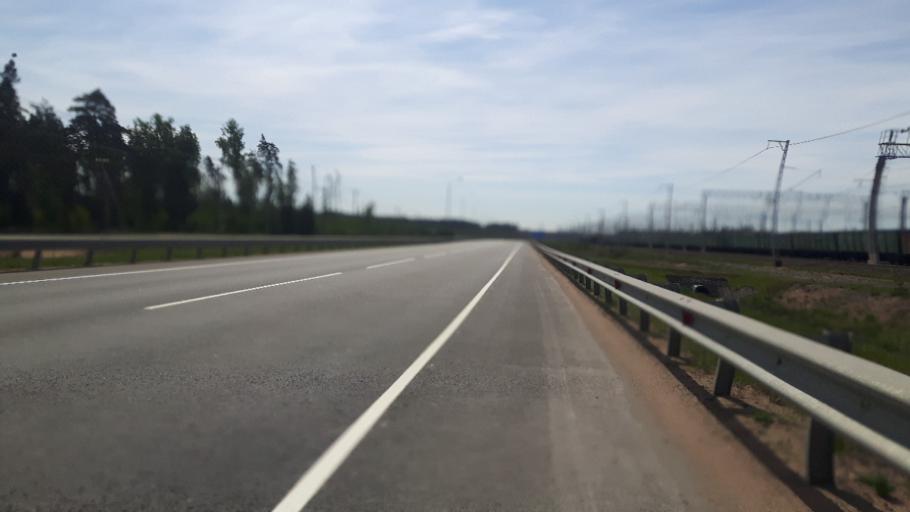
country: RU
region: Leningrad
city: Vistino
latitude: 59.6686
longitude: 28.4333
